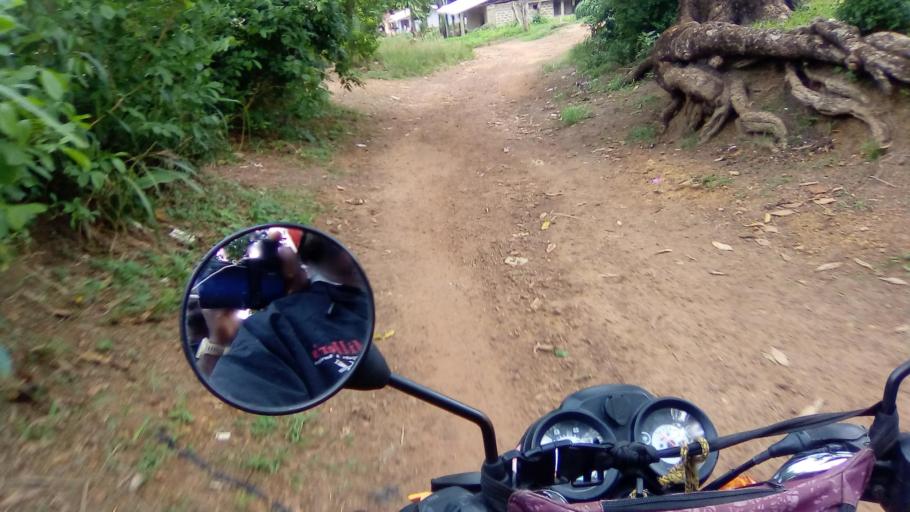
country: SL
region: Southern Province
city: Bo
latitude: 7.9510
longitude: -11.7299
